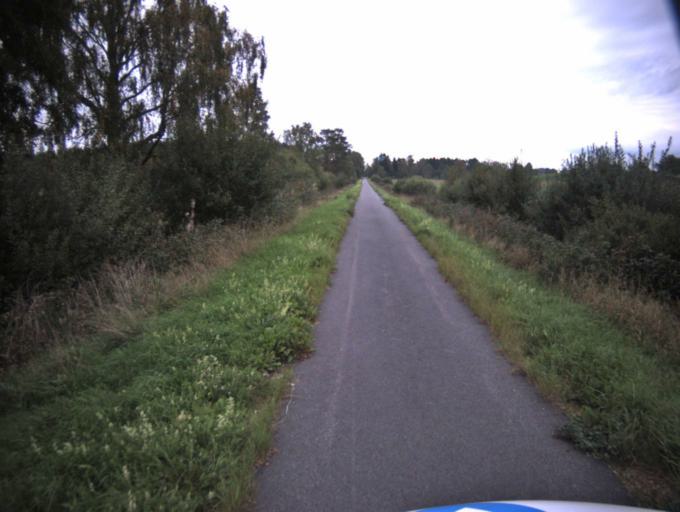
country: SE
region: Vaestra Goetaland
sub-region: Falkopings Kommun
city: Falkoeping
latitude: 58.0023
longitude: 13.5478
